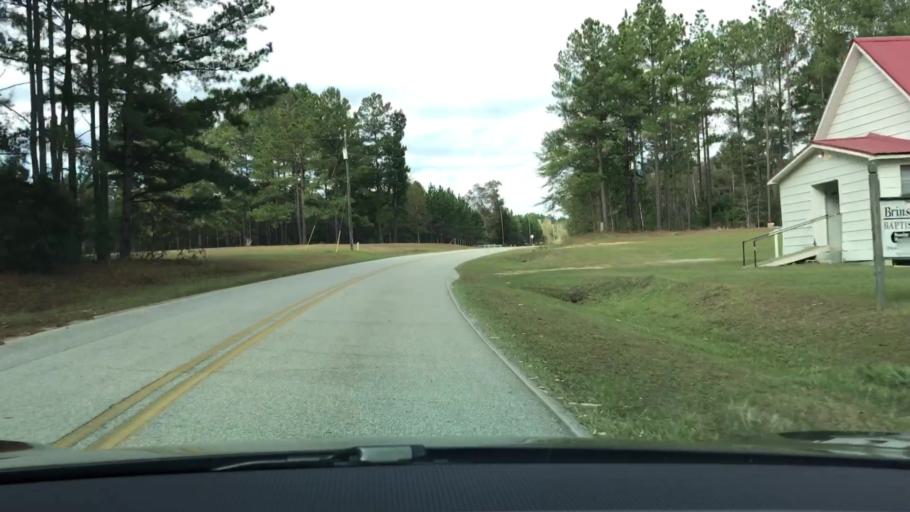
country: US
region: Georgia
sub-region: Jefferson County
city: Wadley
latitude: 32.7991
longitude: -82.3790
